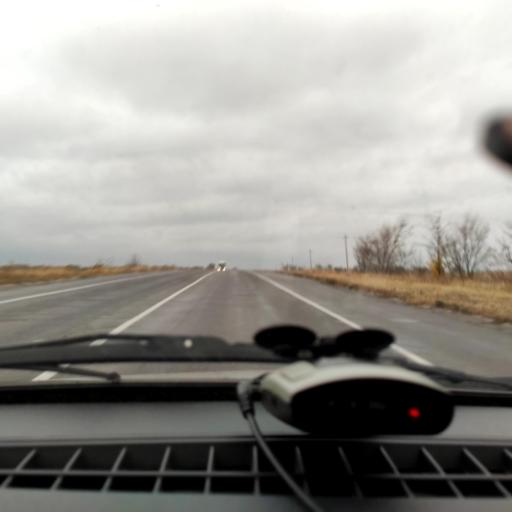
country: RU
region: Voronezj
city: Devitsa
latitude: 51.5740
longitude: 38.9749
